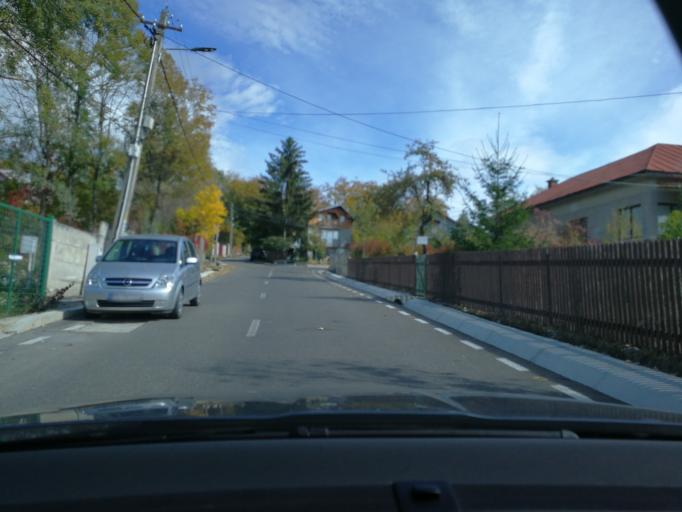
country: RO
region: Prahova
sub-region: Comuna Cornu
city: Cornu de Jos
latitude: 45.1542
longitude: 25.7161
